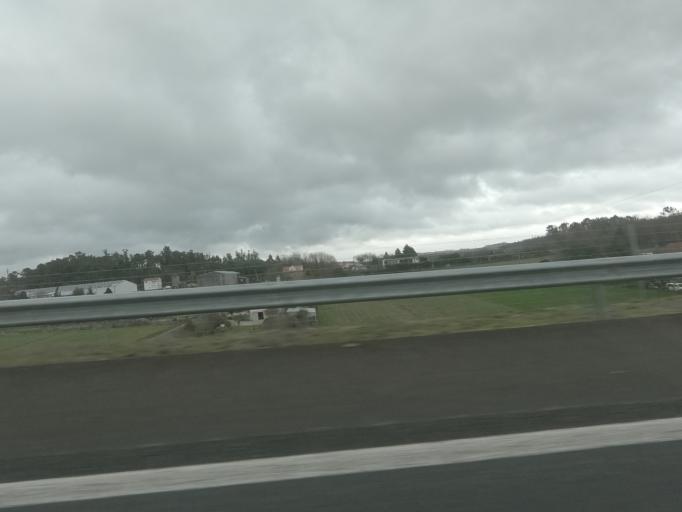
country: ES
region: Galicia
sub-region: Provincia da Coruna
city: Vedra
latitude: 42.8182
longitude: -8.4882
